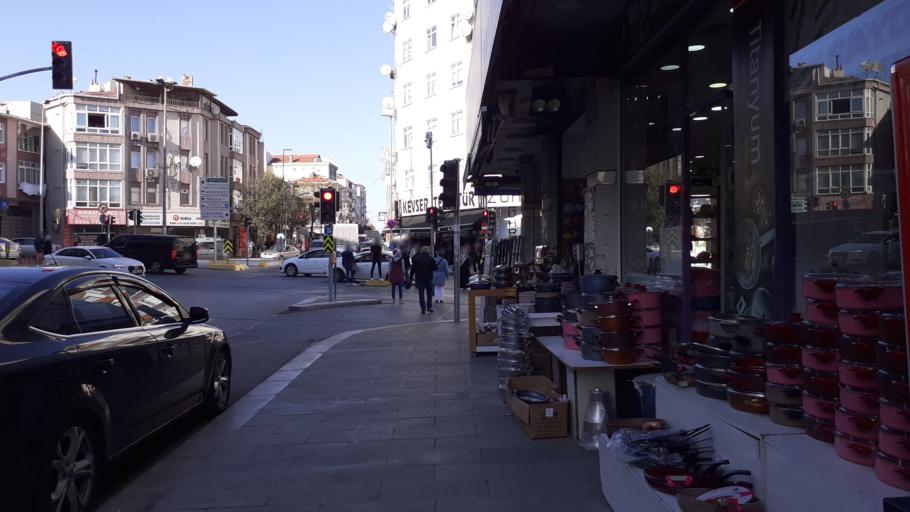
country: TR
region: Istanbul
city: Mahmutbey
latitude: 41.0093
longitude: 28.7988
